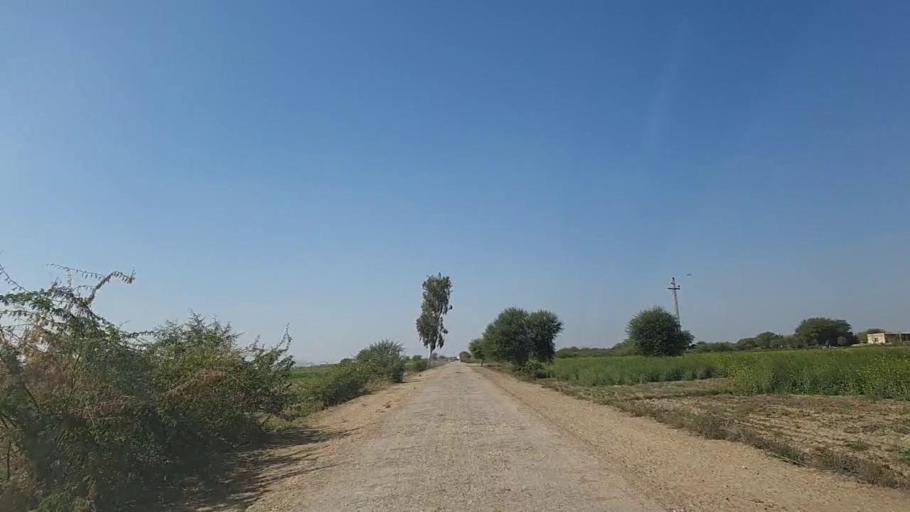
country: PK
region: Sindh
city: Naukot
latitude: 25.0408
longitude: 69.3807
